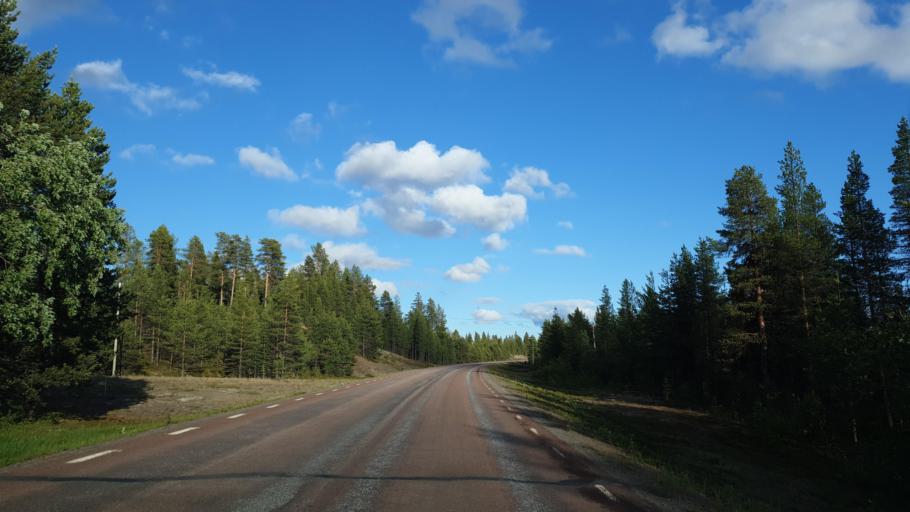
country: SE
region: Norrbotten
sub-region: Arjeplogs Kommun
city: Arjeplog
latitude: 66.0484
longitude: 18.0284
